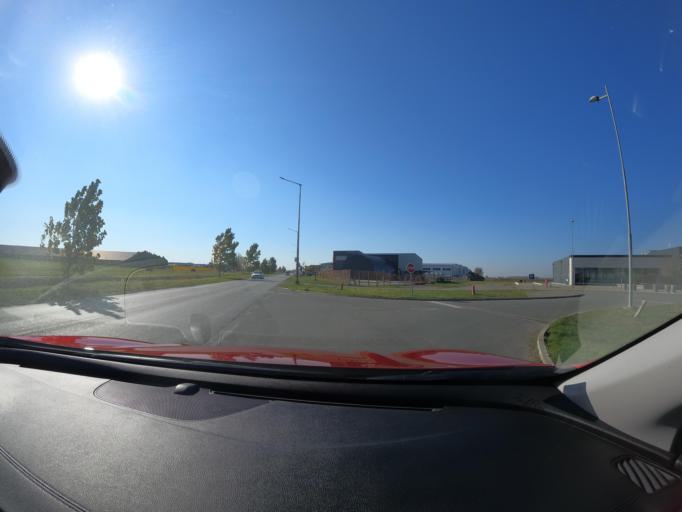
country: RS
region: Autonomna Pokrajina Vojvodina
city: Nova Pazova
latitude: 44.9558
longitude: 20.1998
